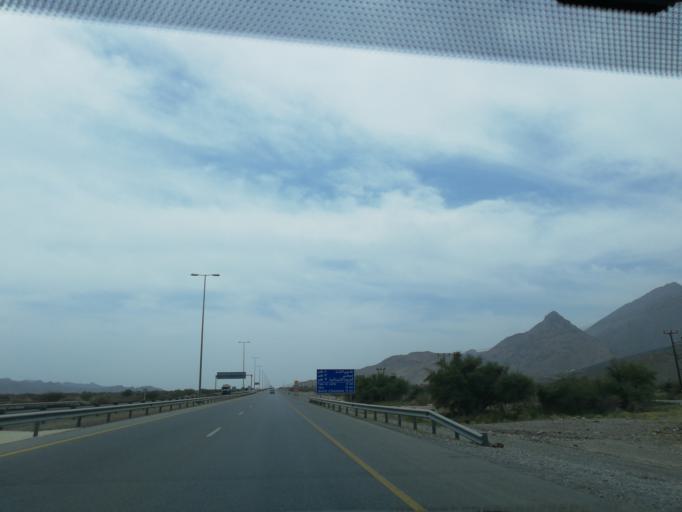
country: OM
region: Muhafazat ad Dakhiliyah
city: Izki
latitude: 23.0877
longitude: 57.8222
